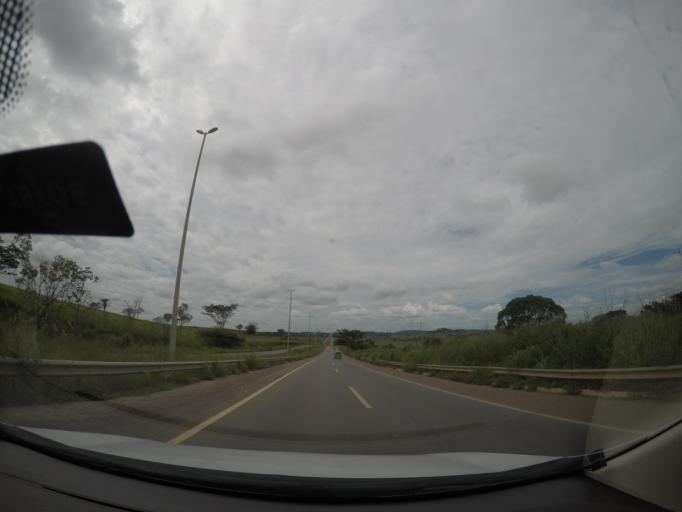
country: BR
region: Goias
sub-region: Inhumas
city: Inhumas
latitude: -16.4081
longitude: -49.4773
